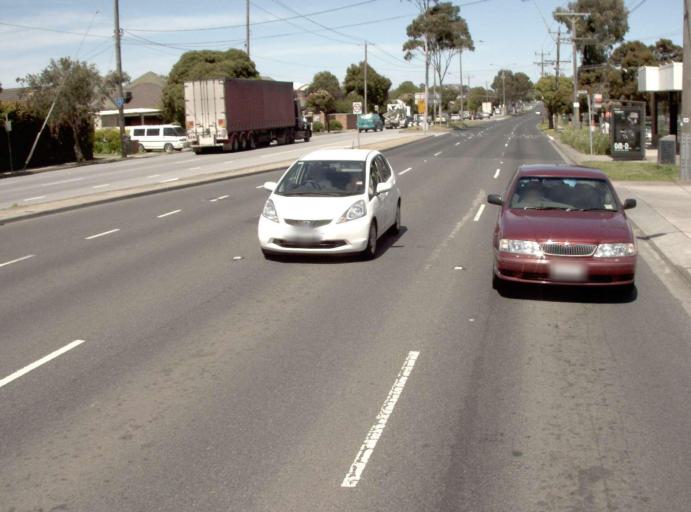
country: AU
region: Victoria
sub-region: Monash
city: Clayton
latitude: -37.9167
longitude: 145.1399
